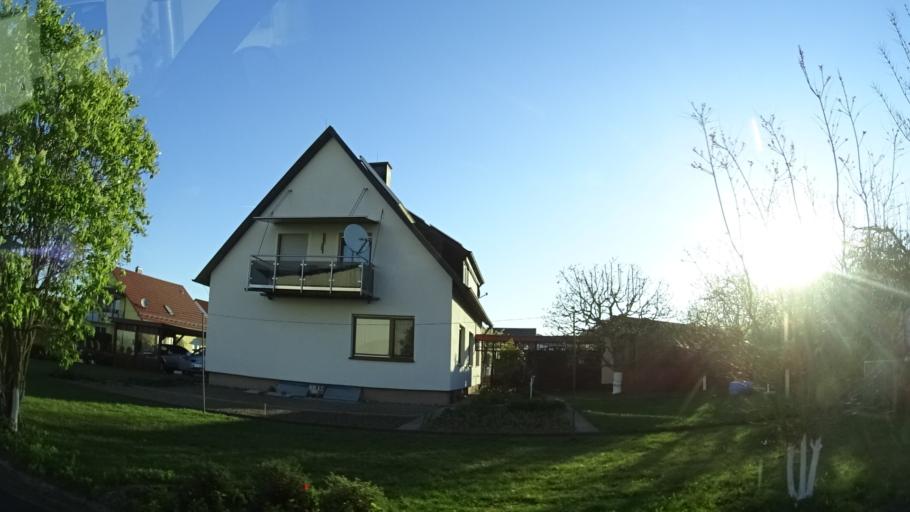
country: DE
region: Baden-Wuerttemberg
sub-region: Regierungsbezirk Stuttgart
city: Wolpertshausen
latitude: 49.1694
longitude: 9.8488
